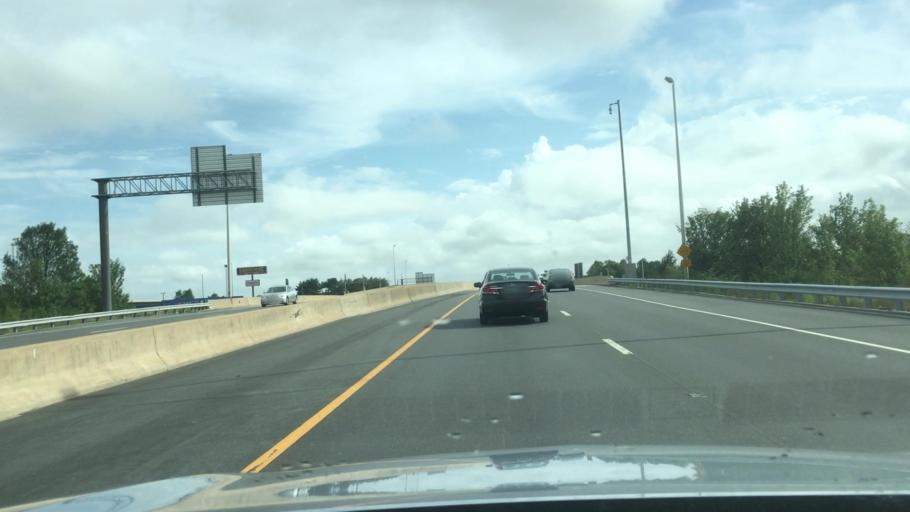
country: US
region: Delaware
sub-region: New Castle County
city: Newport
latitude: 39.6895
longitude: -75.6543
